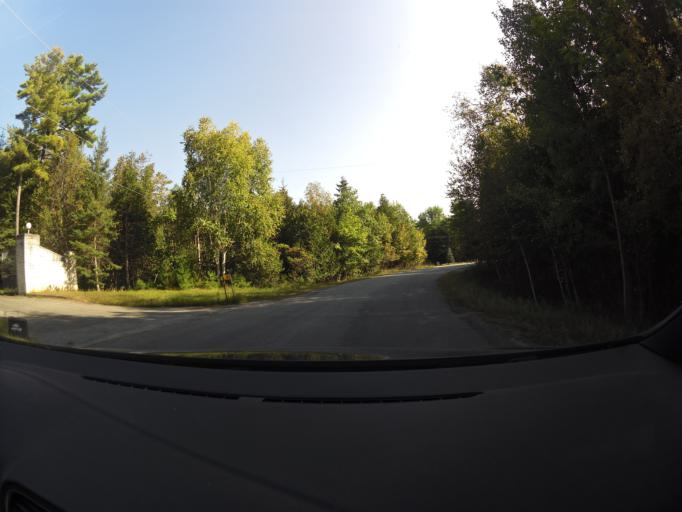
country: CA
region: Ontario
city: Arnprior
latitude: 45.4594
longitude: -76.2762
